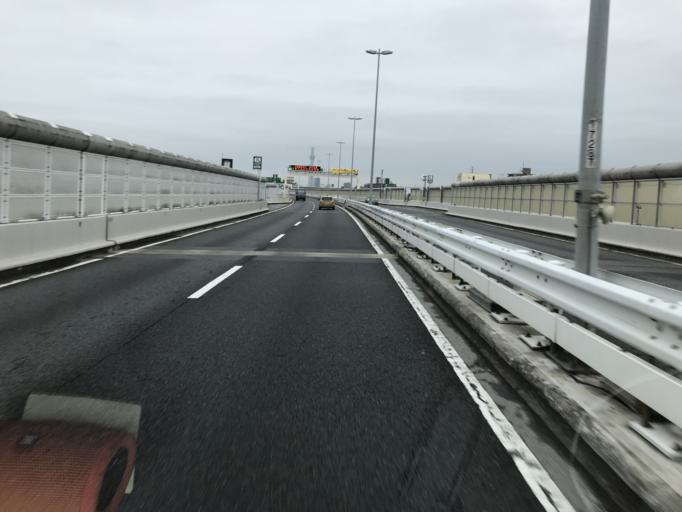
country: JP
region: Tokyo
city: Urayasu
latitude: 35.6984
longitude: 139.8730
